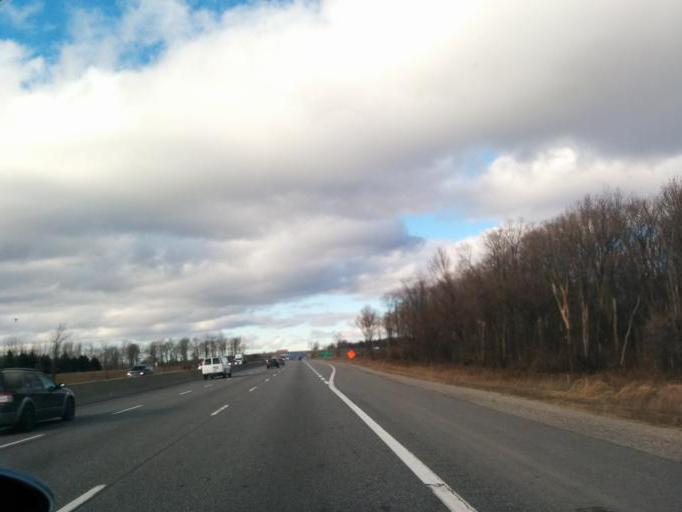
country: CA
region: Ontario
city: Bradford West Gwillimbury
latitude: 43.9967
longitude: -79.5842
